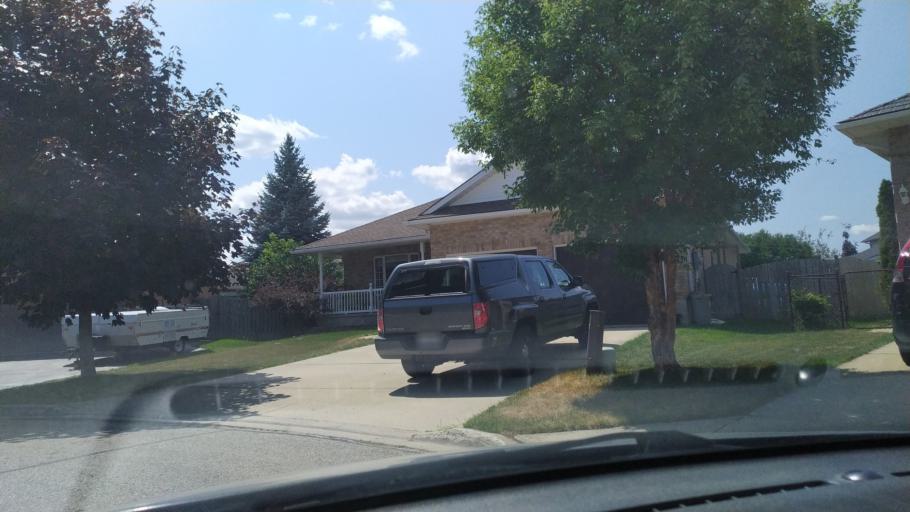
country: CA
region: Ontario
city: Stratford
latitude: 43.3641
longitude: -81.0018
